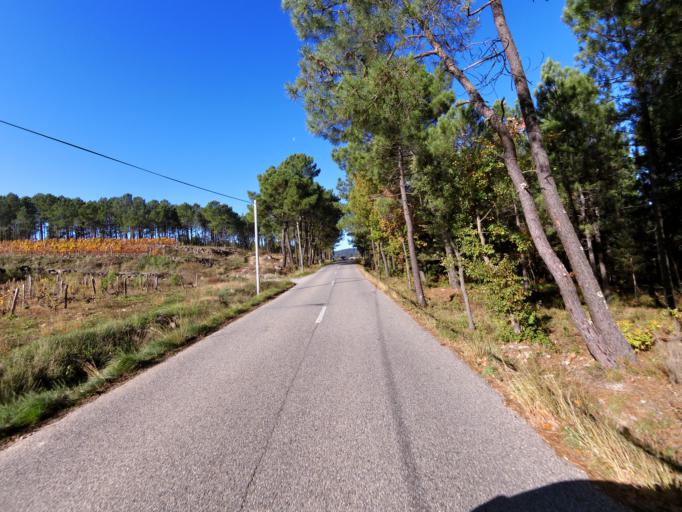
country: FR
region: Rhone-Alpes
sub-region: Departement de l'Ardeche
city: Lablachere
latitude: 44.4792
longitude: 4.1739
